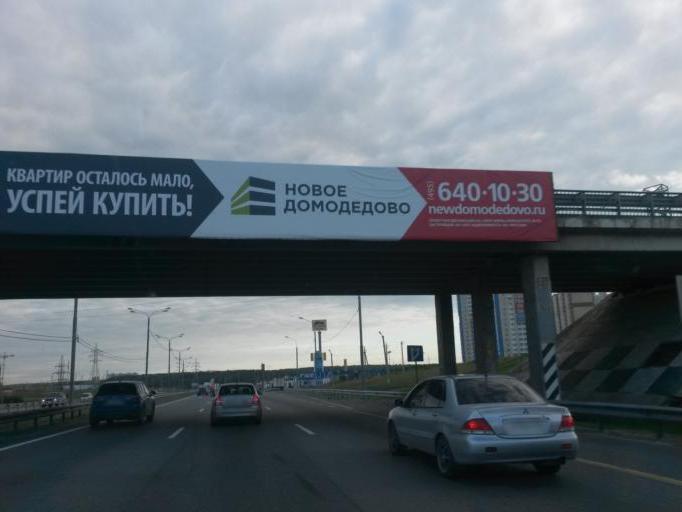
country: RU
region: Moskovskaya
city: Vostryakovo
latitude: 55.3968
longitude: 37.7777
